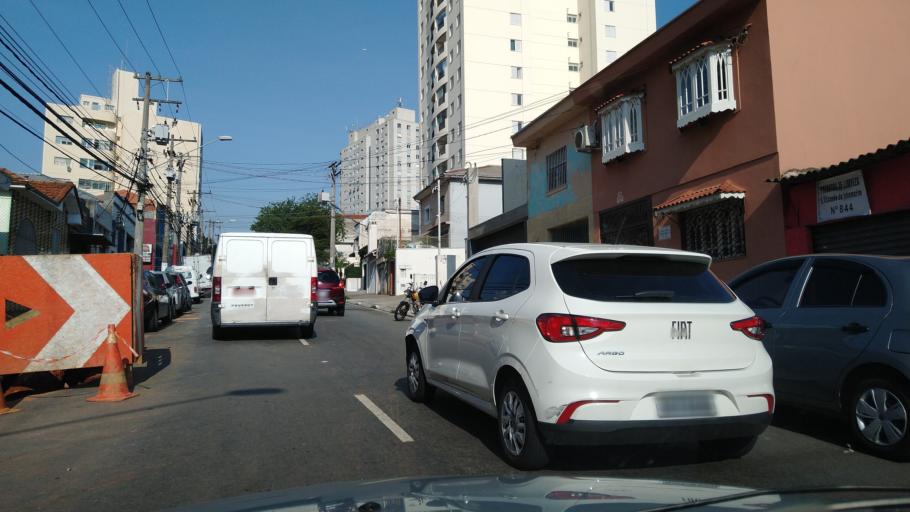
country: BR
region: Sao Paulo
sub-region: Sao Paulo
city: Sao Paulo
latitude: -23.5628
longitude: -46.6007
